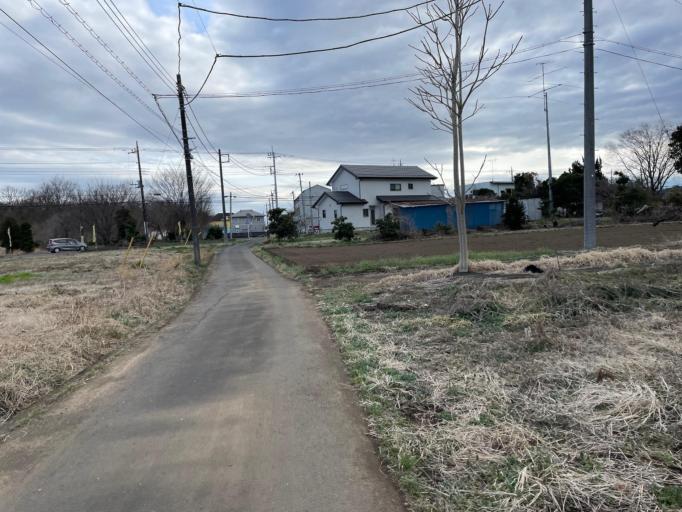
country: JP
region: Saitama
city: Sakado
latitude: 35.9549
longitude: 139.3449
